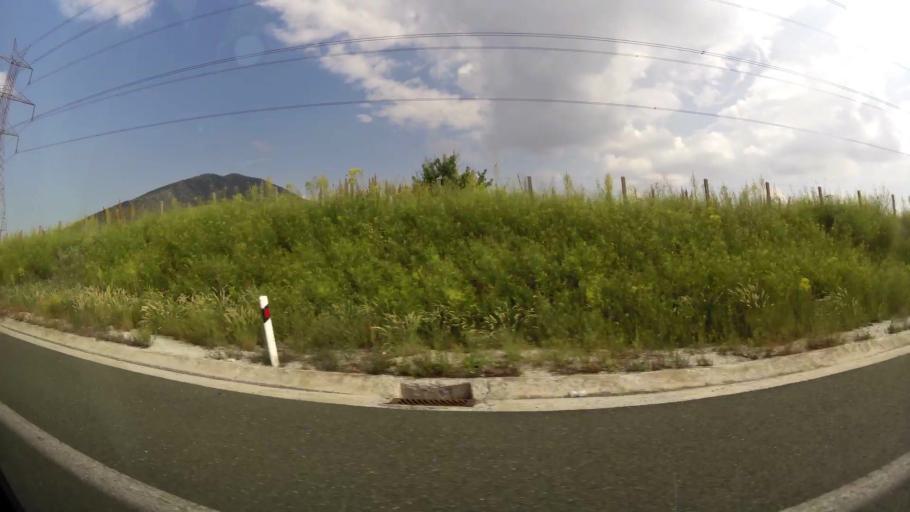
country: GR
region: West Macedonia
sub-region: Nomos Kozanis
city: Kleitos
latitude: 40.3658
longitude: 21.8651
